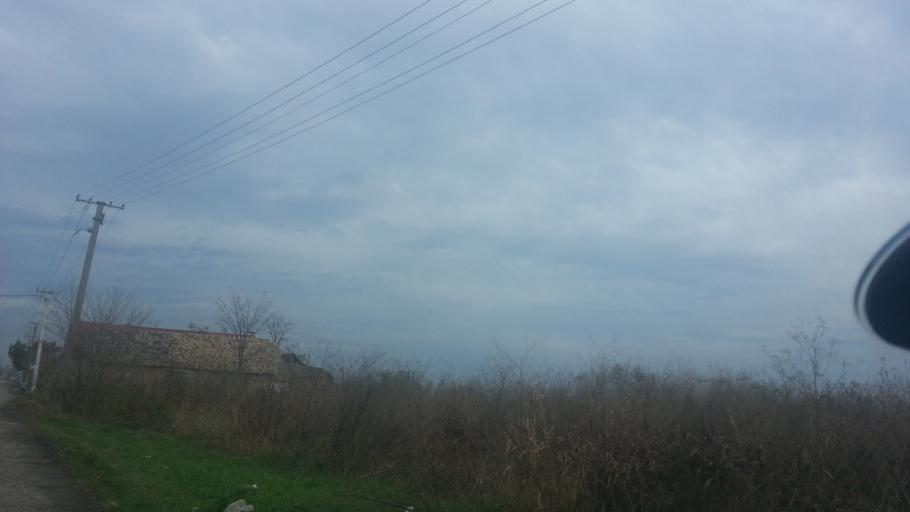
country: RS
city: Golubinci
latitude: 44.9815
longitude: 20.0807
